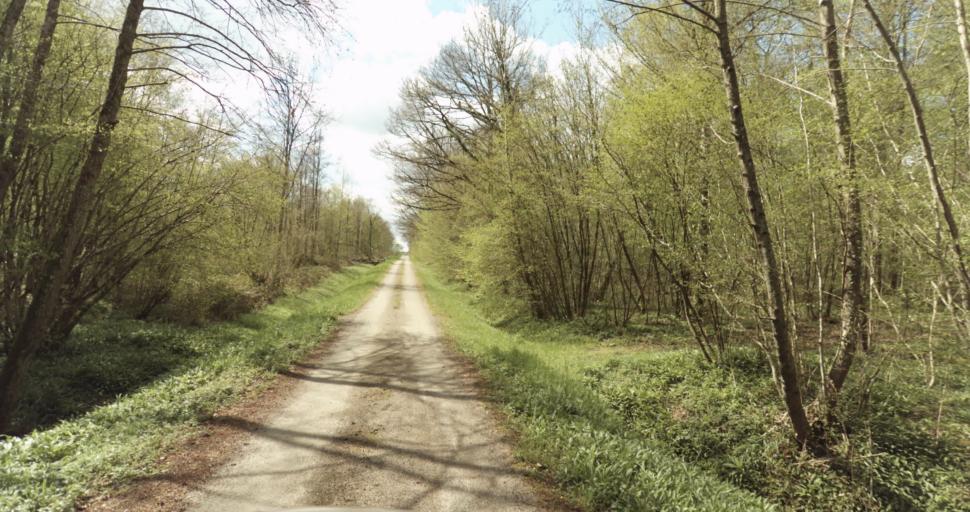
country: FR
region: Franche-Comte
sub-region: Departement du Jura
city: Champvans
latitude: 47.1603
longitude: 5.4395
